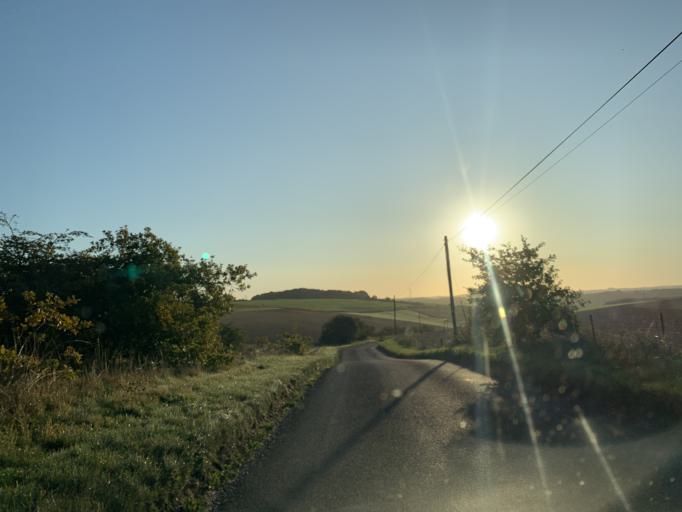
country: GB
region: England
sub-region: Wiltshire
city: Woodford
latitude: 51.1283
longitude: -1.8543
